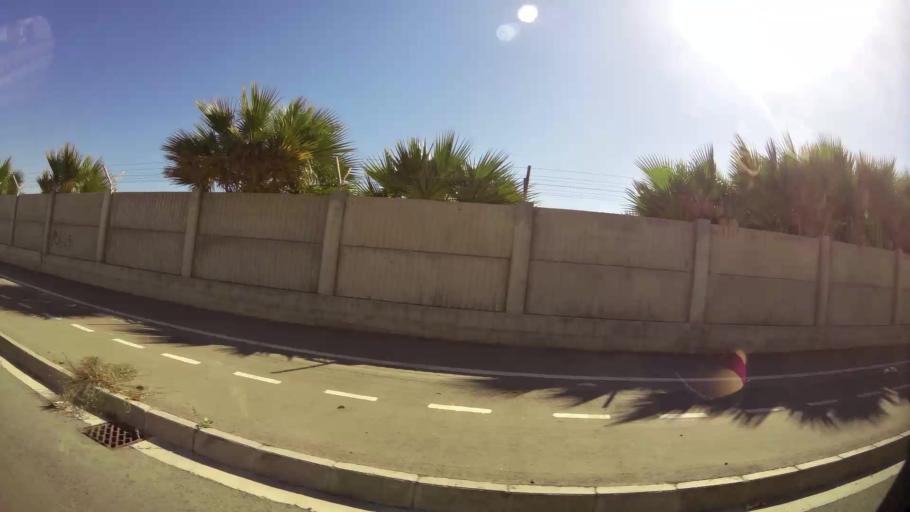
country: CY
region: Larnaka
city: Larnaca
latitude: 34.9316
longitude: 33.6388
